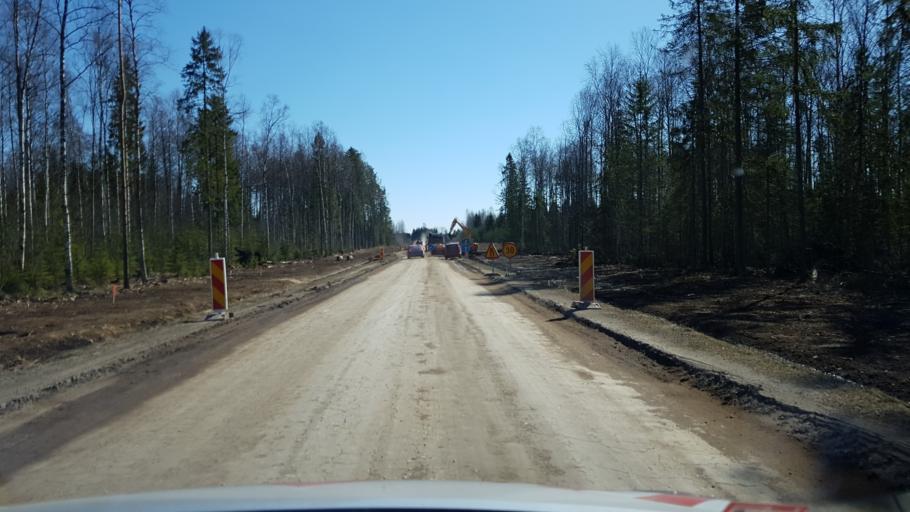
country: EE
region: Jogevamaa
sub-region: Mustvee linn
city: Mustvee
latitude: 59.0396
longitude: 26.6721
